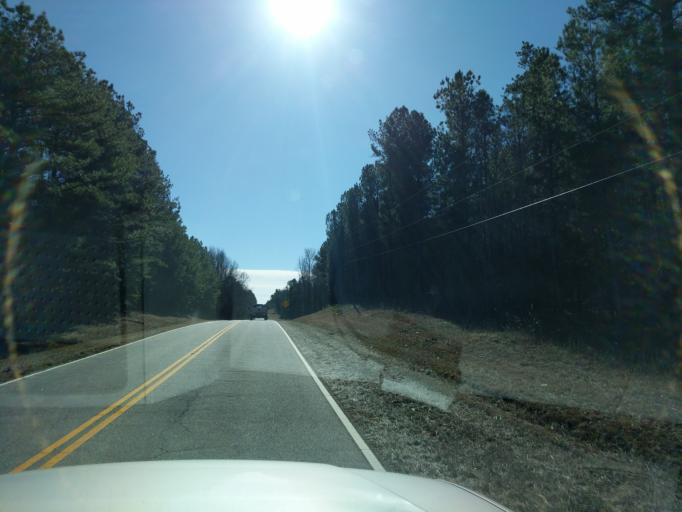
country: US
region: South Carolina
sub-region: Saluda County
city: Saluda
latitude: 34.1419
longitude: -81.8452
